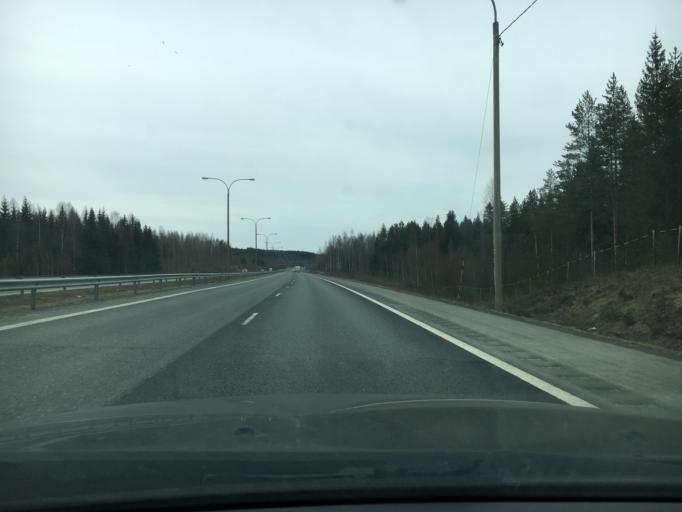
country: FI
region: Northern Savo
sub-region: Kuopio
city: Kuopio
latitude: 62.7891
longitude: 27.5941
